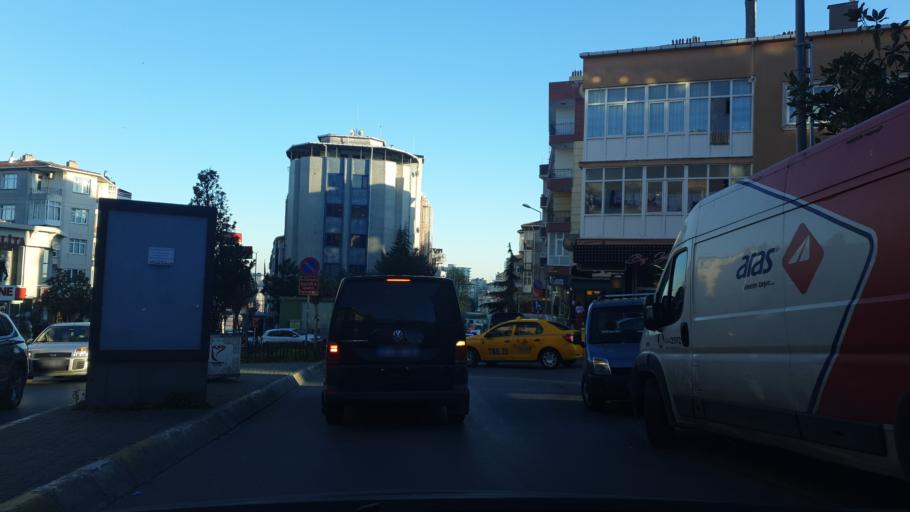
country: TR
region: Istanbul
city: merter keresteciler
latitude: 41.0182
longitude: 28.8757
